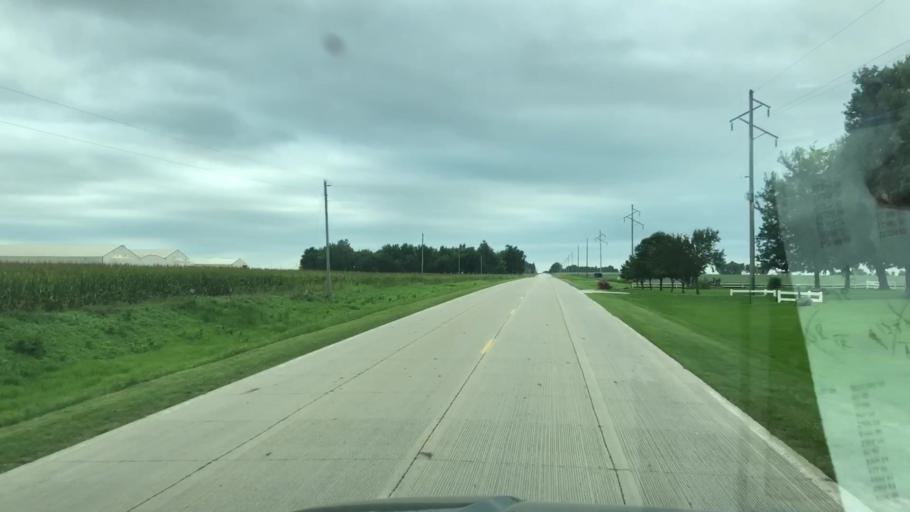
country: US
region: Iowa
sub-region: O'Brien County
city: Sheldon
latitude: 43.1817
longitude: -95.9801
